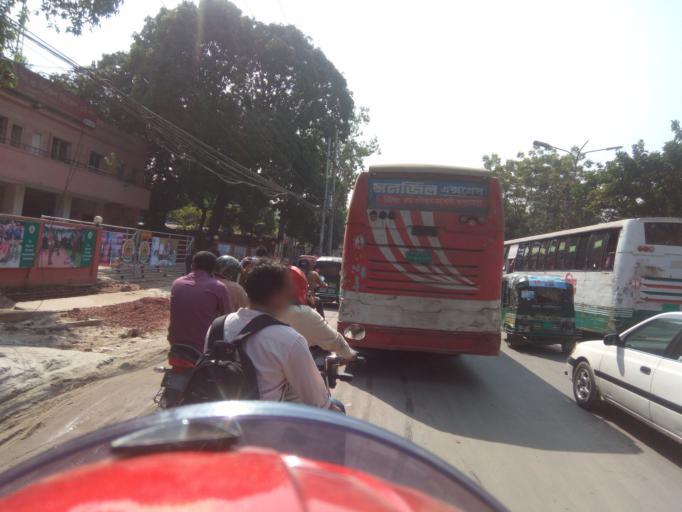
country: BD
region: Dhaka
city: Paltan
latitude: 23.7647
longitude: 90.4004
